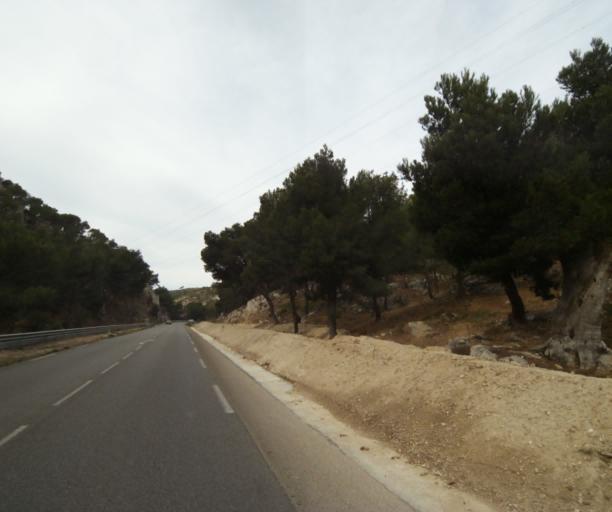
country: FR
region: Provence-Alpes-Cote d'Azur
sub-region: Departement des Bouches-du-Rhone
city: Le Rove
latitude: 43.3639
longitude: 5.2666
